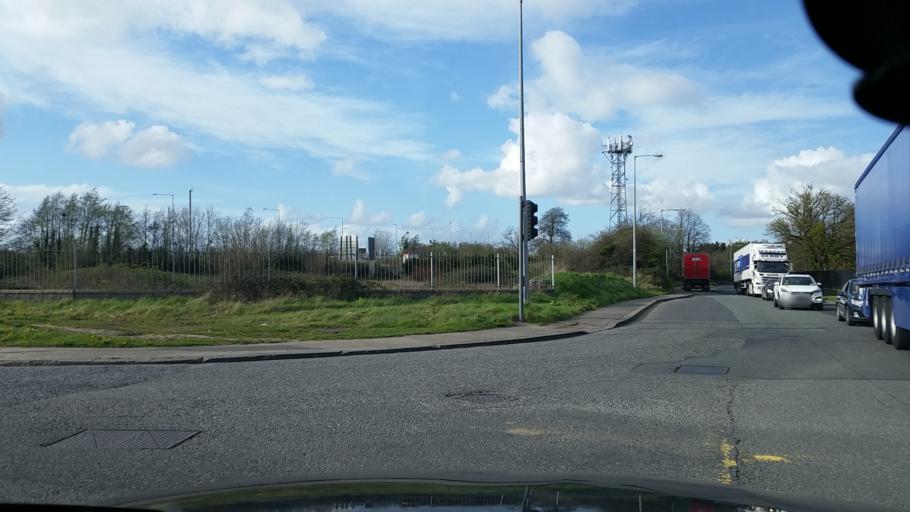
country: IE
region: Leinster
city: Ballymun
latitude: 53.4069
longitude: -6.2623
